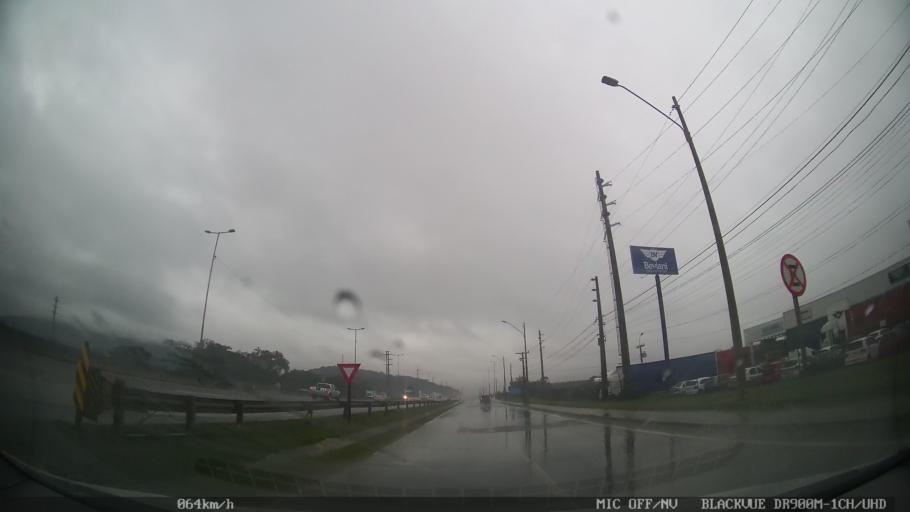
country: BR
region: Santa Catarina
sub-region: Itajai
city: Itajai
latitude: -26.9100
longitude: -48.7129
